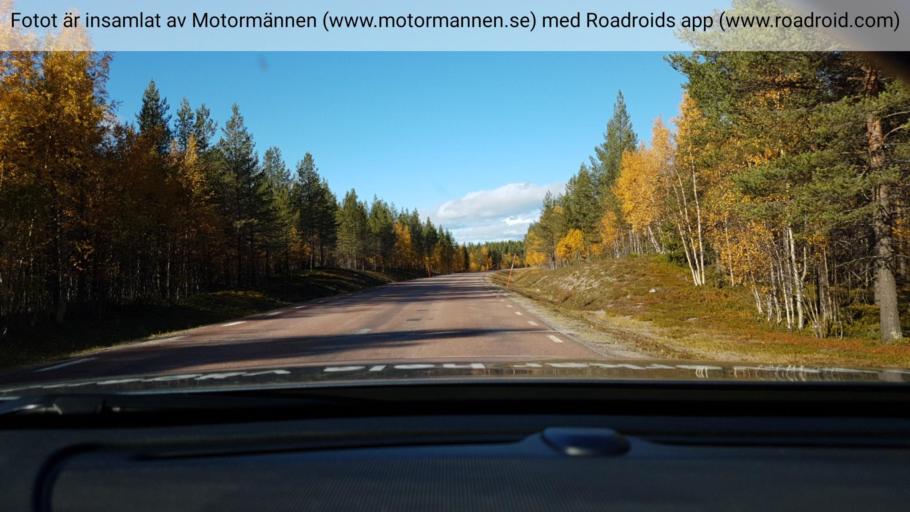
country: SE
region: Norrbotten
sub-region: Arjeplogs Kommun
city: Arjeplog
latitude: 66.0031
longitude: 18.1186
